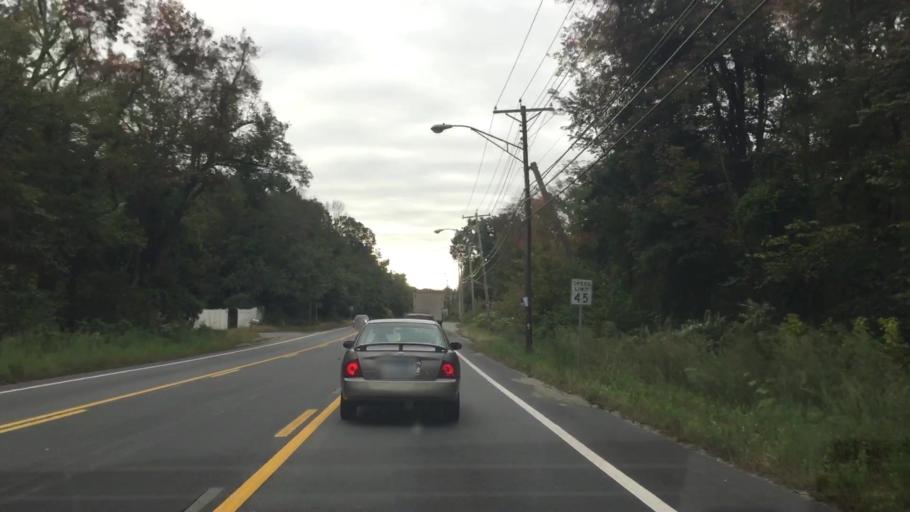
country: US
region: Massachusetts
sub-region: Essex County
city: Andover
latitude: 42.6520
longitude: -71.0966
